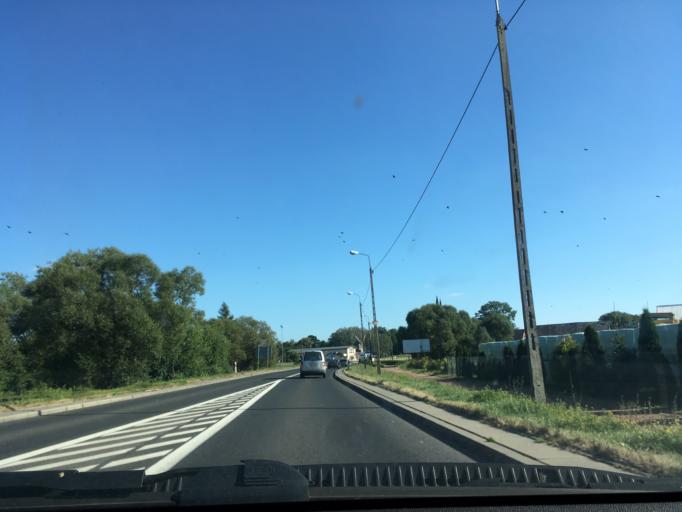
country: PL
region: Podlasie
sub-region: Powiat sokolski
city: Suchowola
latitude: 53.4460
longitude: 23.0930
